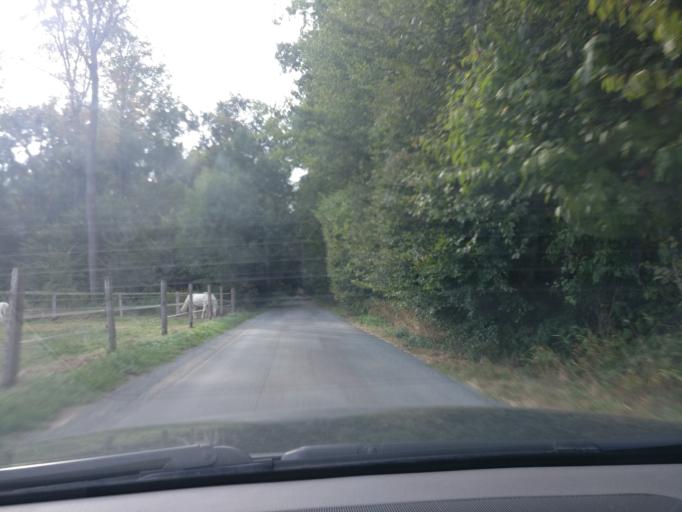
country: DE
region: Lower Saxony
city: Melle
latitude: 52.1729
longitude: 8.3548
